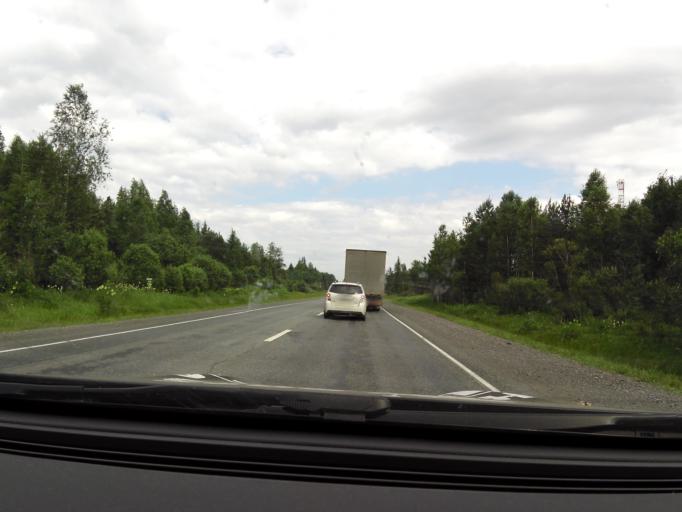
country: RU
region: Sverdlovsk
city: Nizhniye Sergi
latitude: 56.8242
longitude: 59.2873
